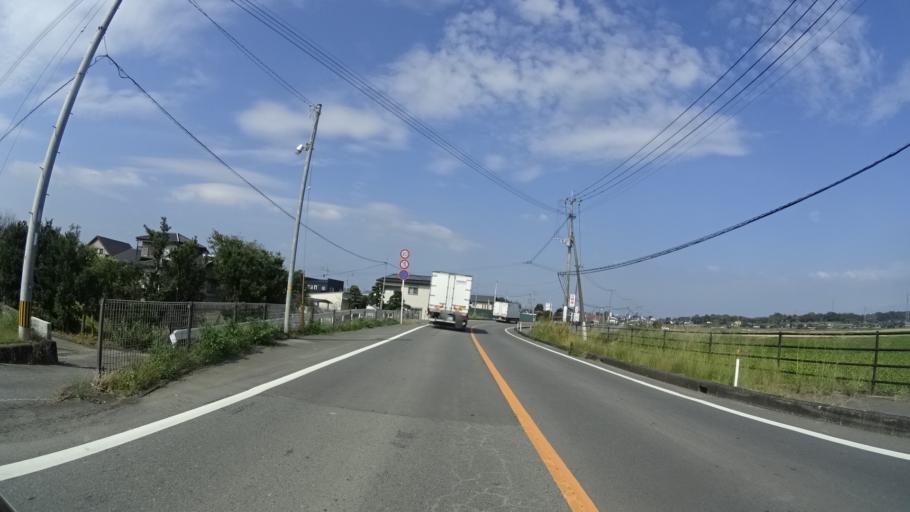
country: JP
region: Kumamoto
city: Kumamoto
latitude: 32.7381
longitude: 130.7726
